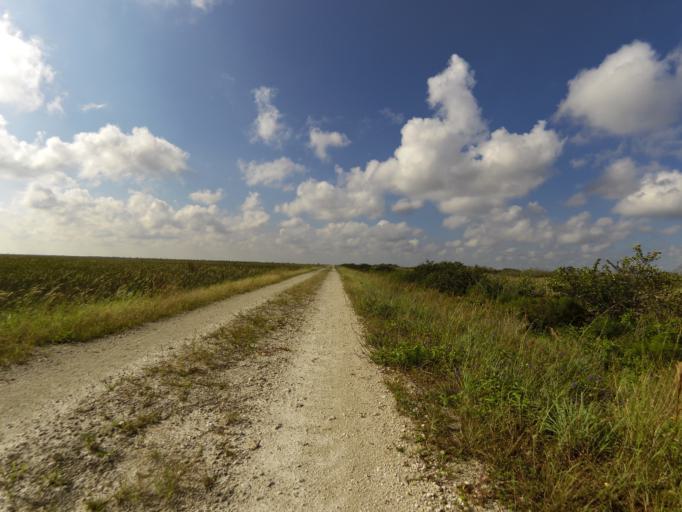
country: US
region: Florida
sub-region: Broward County
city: Weston
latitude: 26.0312
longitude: -80.4950
